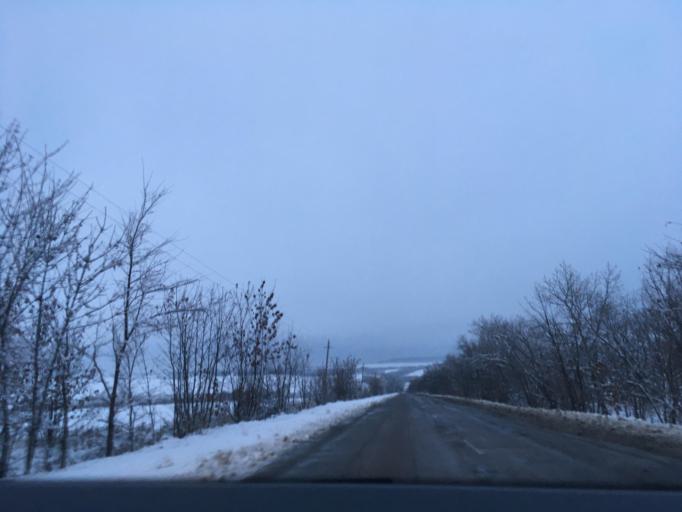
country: RU
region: Voronezj
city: Verkhniy Mamon
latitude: 50.0490
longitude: 40.2422
